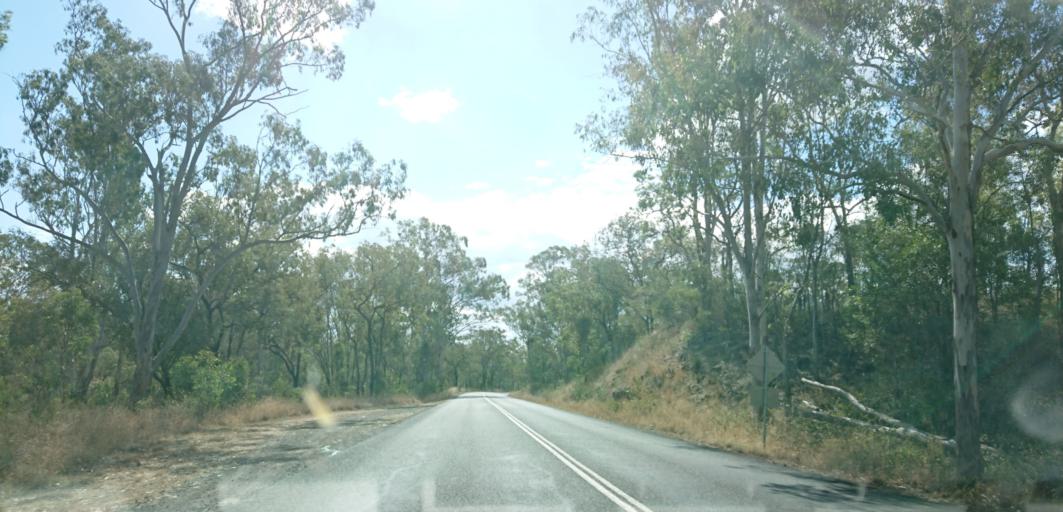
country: AU
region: Queensland
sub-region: Toowoomba
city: Top Camp
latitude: -27.8143
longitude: 152.1068
